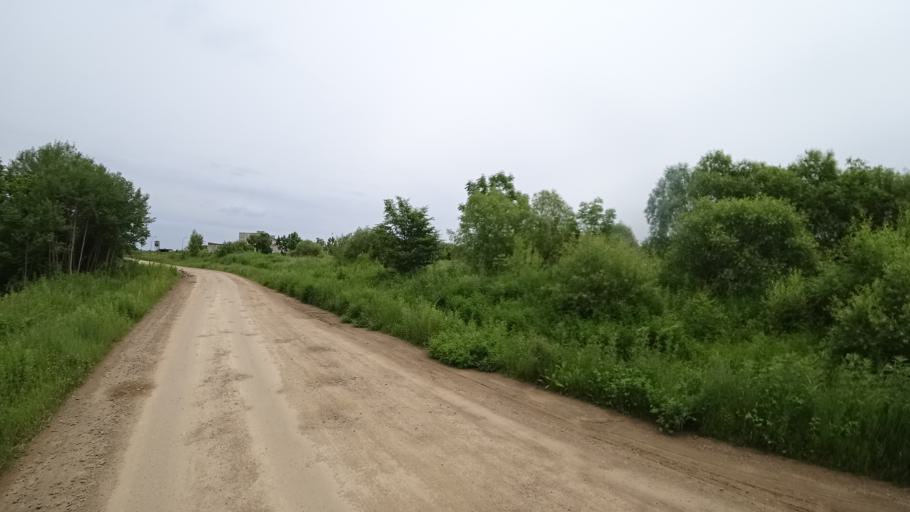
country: RU
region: Primorskiy
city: Arsen'yev
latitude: 44.1981
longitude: 133.3086
